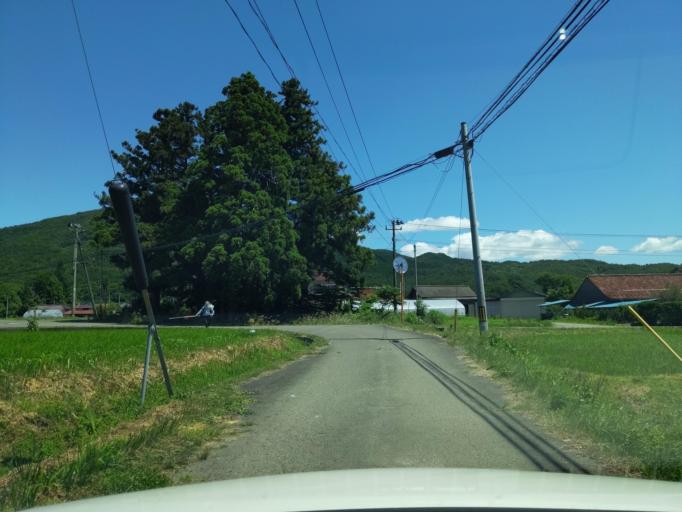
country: JP
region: Fukushima
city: Koriyama
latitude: 37.4097
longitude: 140.2371
